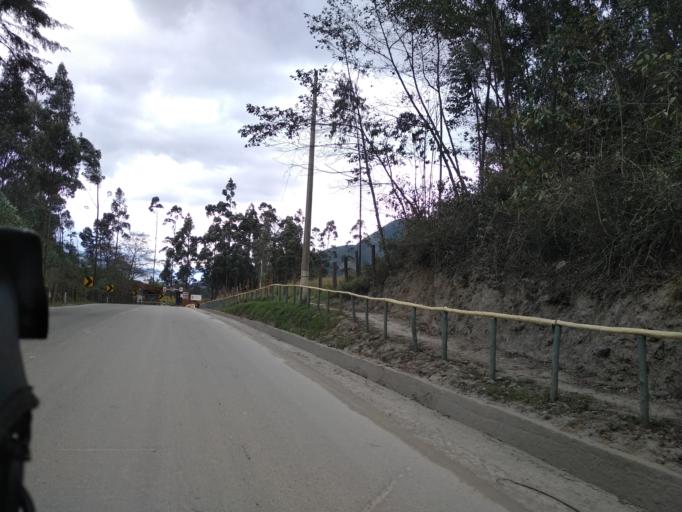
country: EC
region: Loja
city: Loja
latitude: -4.0838
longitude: -79.2055
